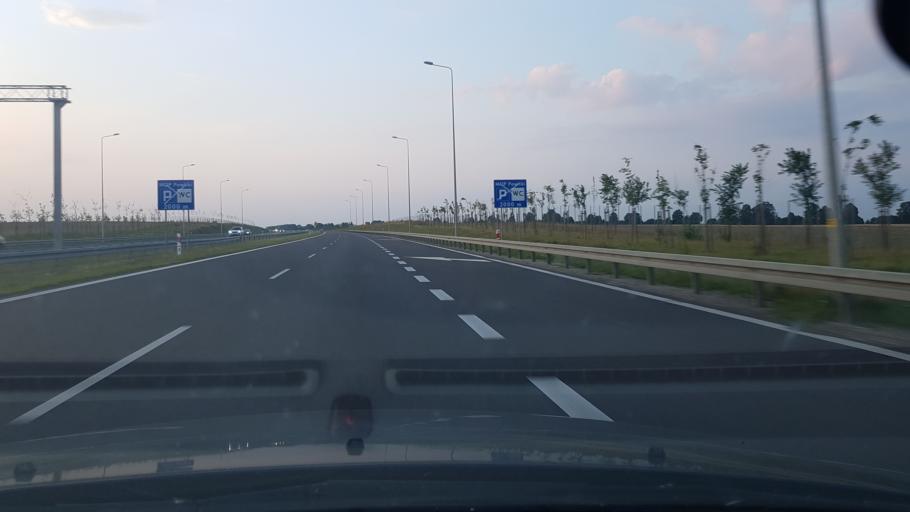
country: PL
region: Warmian-Masurian Voivodeship
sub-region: Powiat nidzicki
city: Nidzica
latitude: 53.2800
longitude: 20.4383
